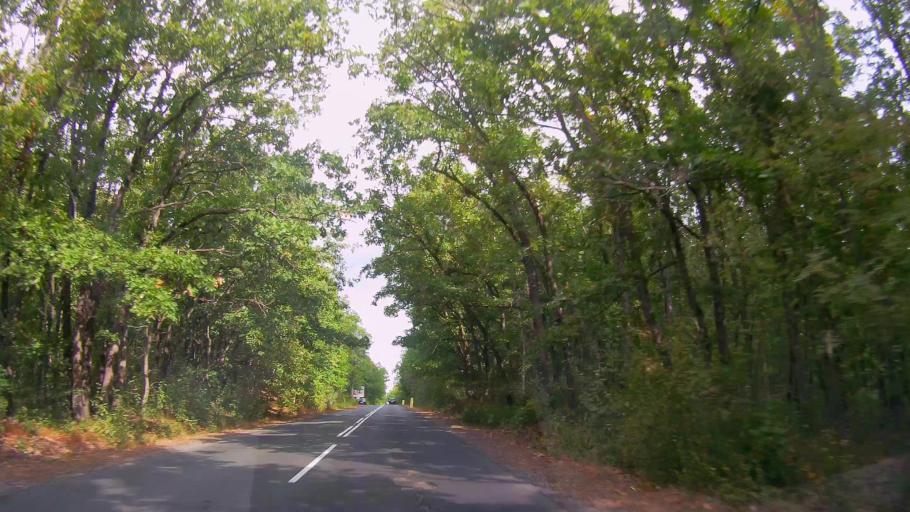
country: BG
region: Burgas
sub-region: Obshtina Primorsko
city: Primorsko
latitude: 42.2821
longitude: 27.7379
